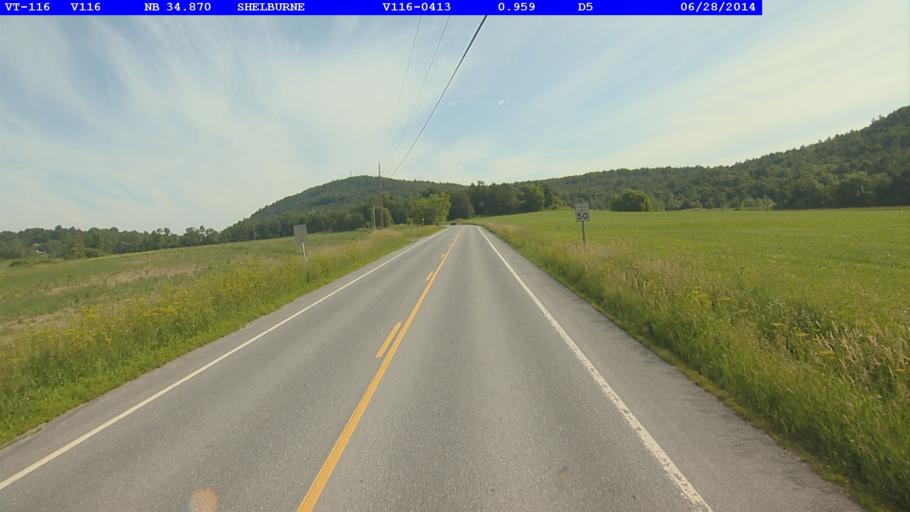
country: US
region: Vermont
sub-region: Chittenden County
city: Hinesburg
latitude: 44.3926
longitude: -73.1414
